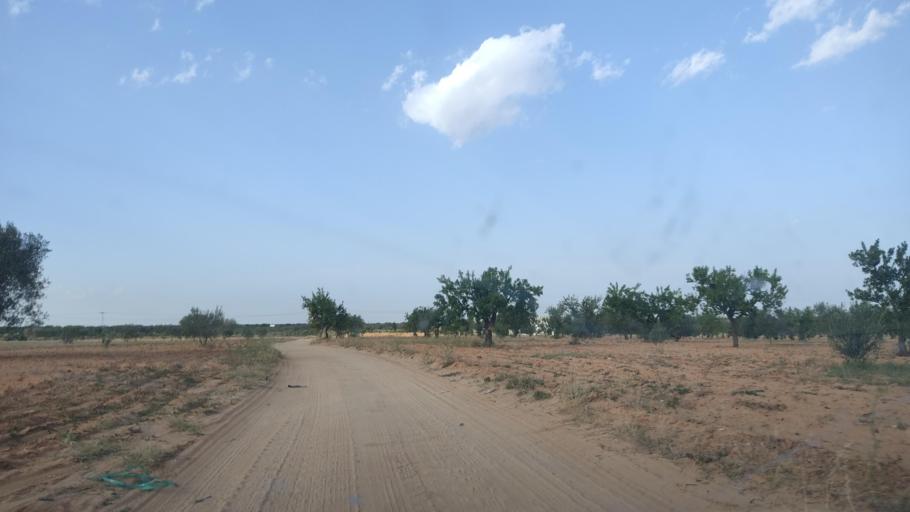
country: TN
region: Safaqis
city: Sfax
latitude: 34.8575
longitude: 10.5993
